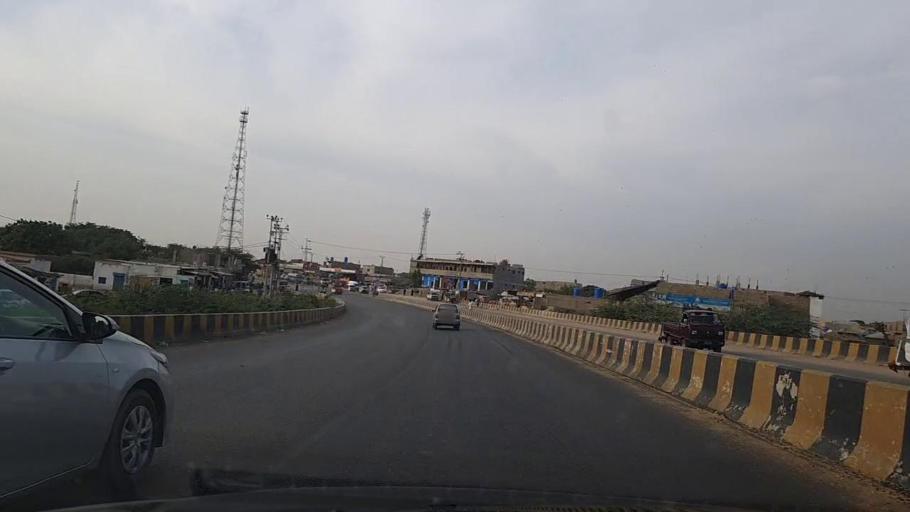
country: PK
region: Sindh
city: Gharo
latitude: 24.8468
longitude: 67.4304
